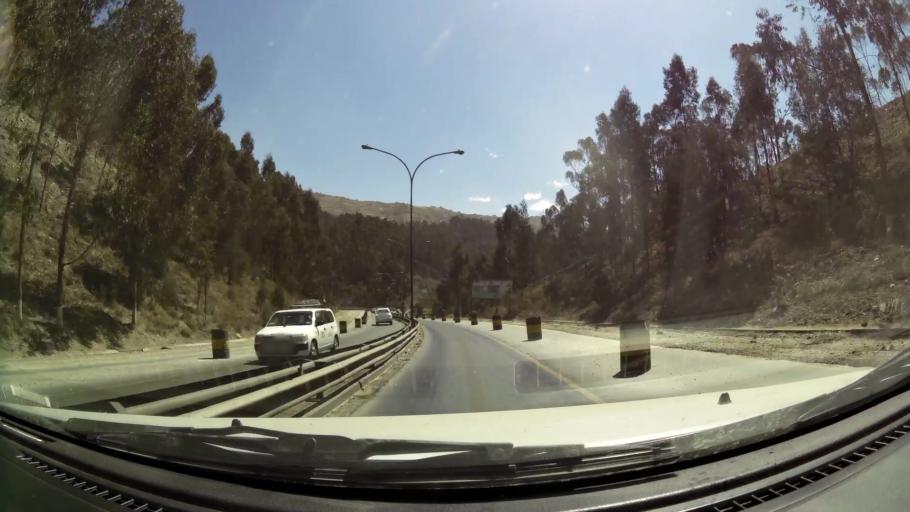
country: BO
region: La Paz
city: La Paz
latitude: -16.4748
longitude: -68.1594
